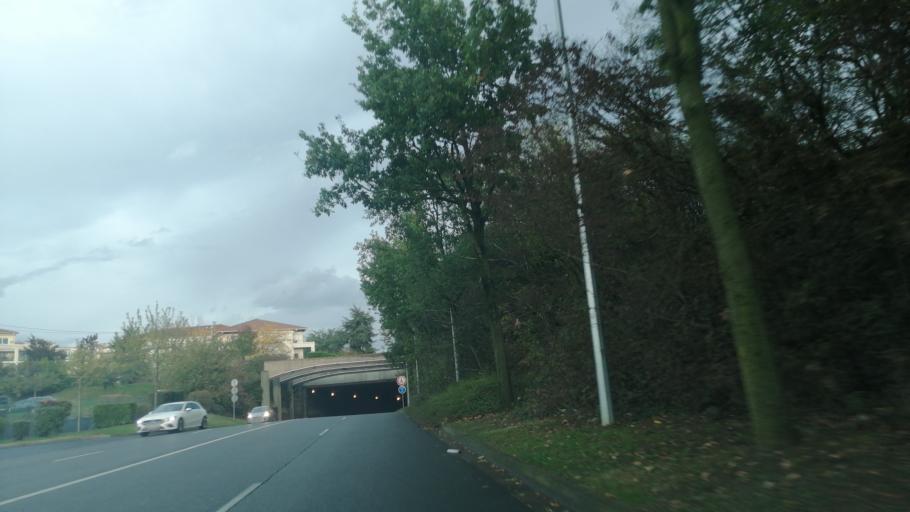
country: FR
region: Rhone-Alpes
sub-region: Departement du Rhone
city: Ecully
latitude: 45.7872
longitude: 4.7778
